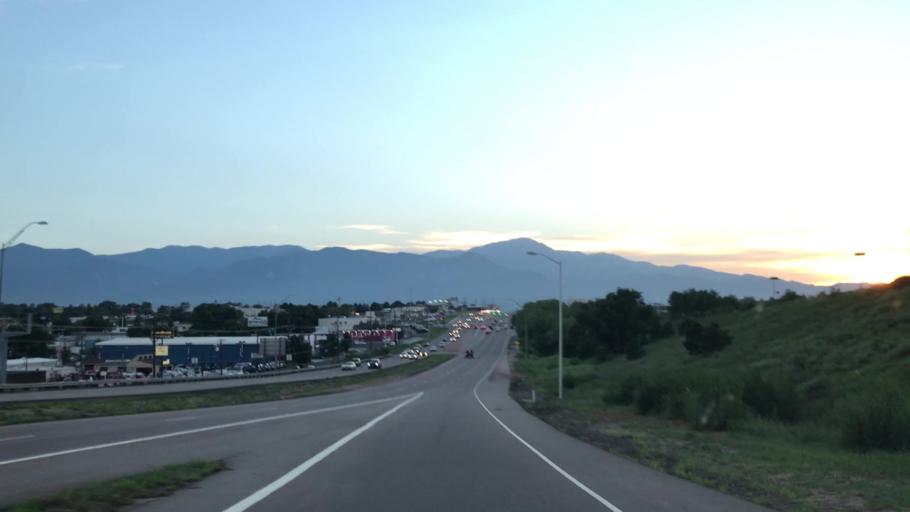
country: US
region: Colorado
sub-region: El Paso County
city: Colorado Springs
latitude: 38.8399
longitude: -104.7610
